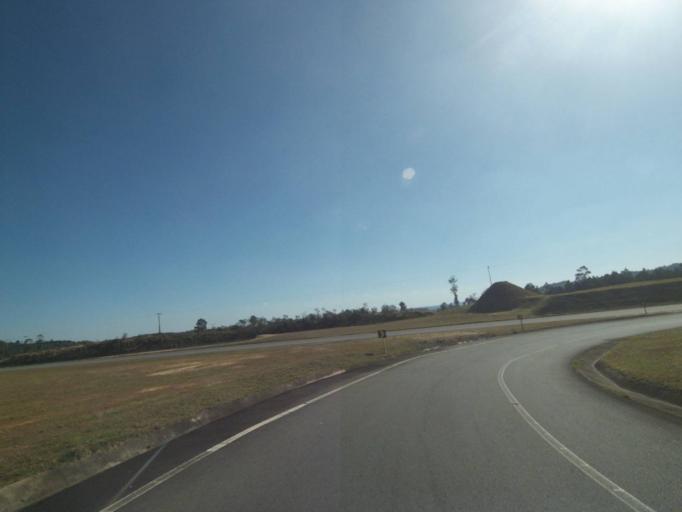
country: BR
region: Parana
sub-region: Tibagi
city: Tibagi
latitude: -24.8166
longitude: -50.4872
